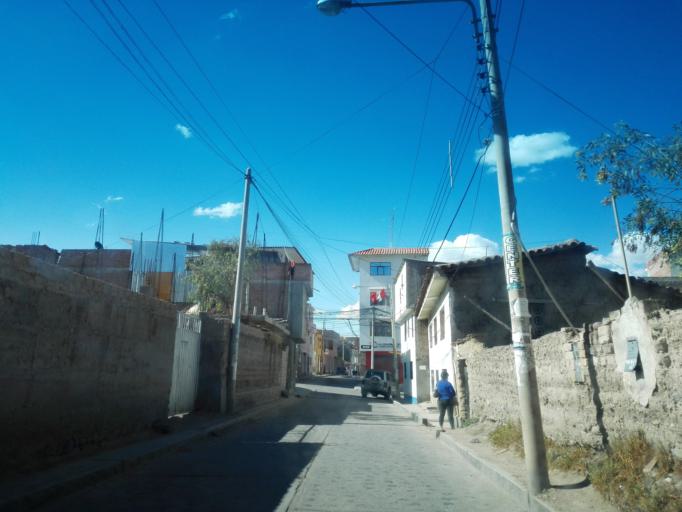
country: PE
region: Ayacucho
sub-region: Provincia de Huamanga
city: Ayacucho
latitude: -13.1570
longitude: -74.2292
